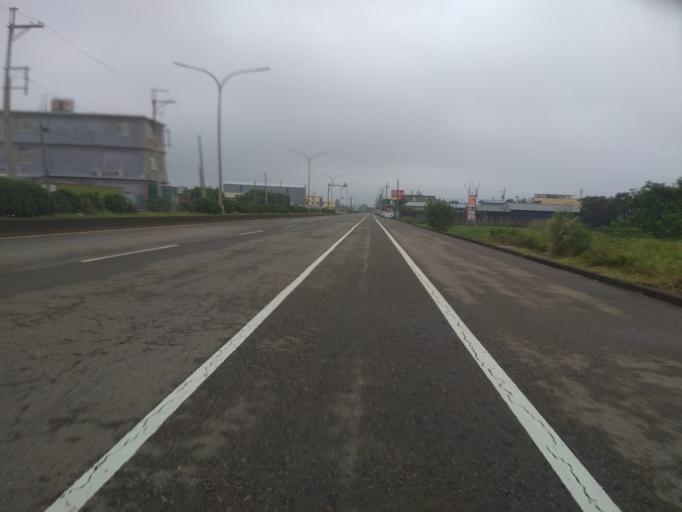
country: TW
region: Taiwan
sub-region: Hsinchu
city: Zhubei
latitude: 25.0265
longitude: 121.0798
